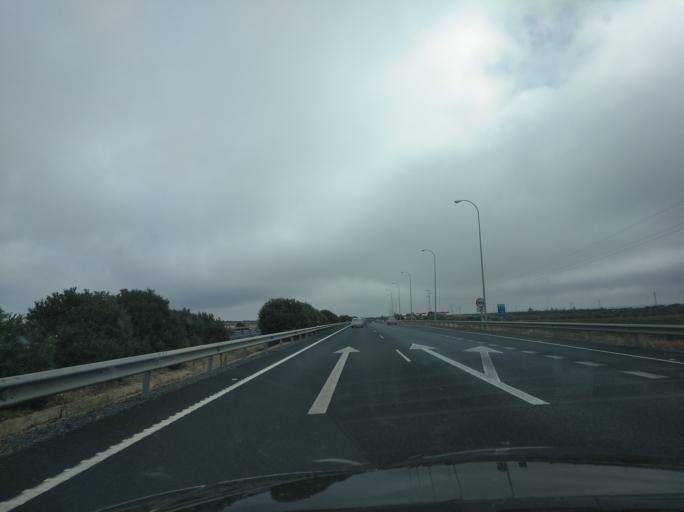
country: ES
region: Andalusia
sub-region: Provincia de Huelva
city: San Juan del Puerto
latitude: 37.3310
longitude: -6.8092
